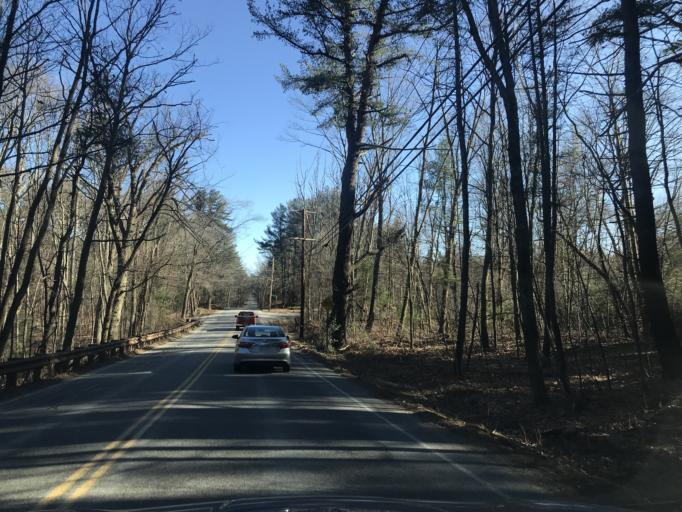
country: US
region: Massachusetts
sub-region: Essex County
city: Groveland
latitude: 42.7118
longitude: -71.0335
